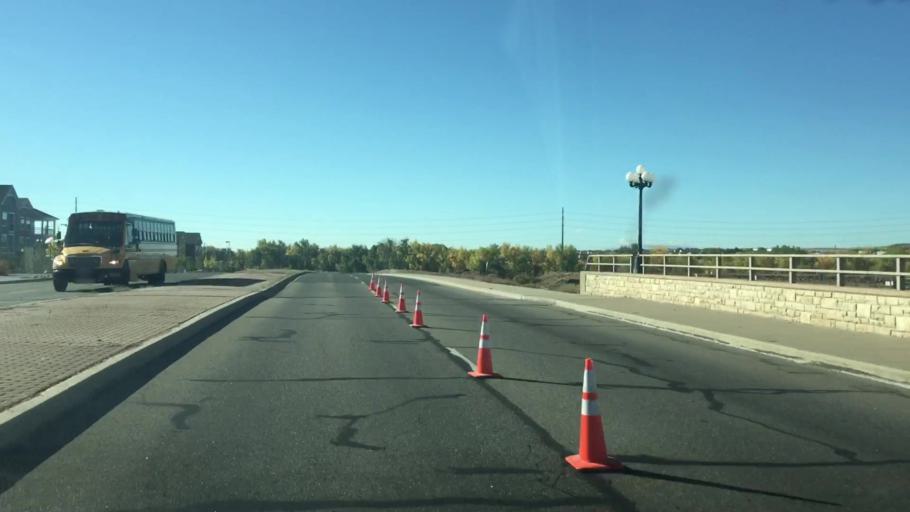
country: US
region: Colorado
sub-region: Douglas County
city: Parker
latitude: 39.5164
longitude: -104.7747
